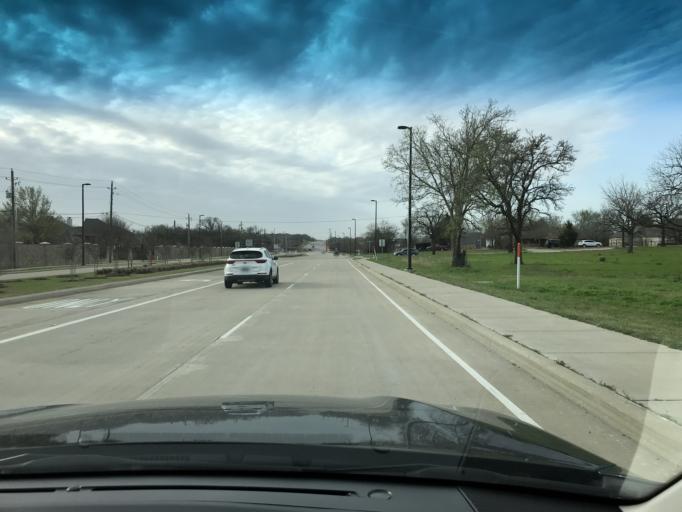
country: US
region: Texas
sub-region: Tarrant County
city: Southlake
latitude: 32.9425
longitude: -97.1860
